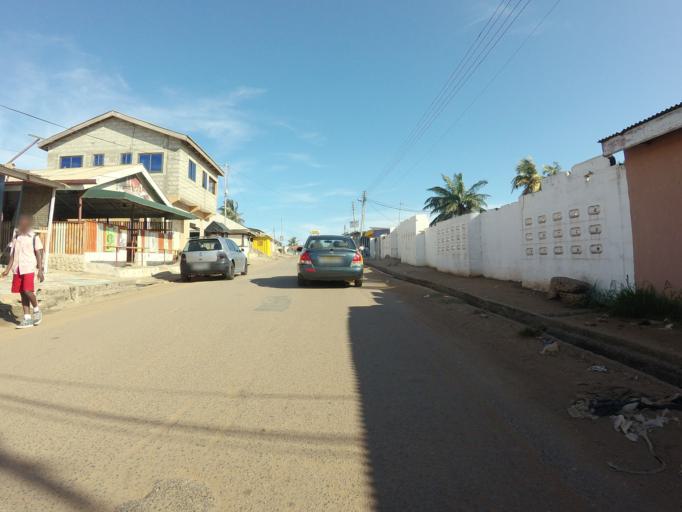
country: GH
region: Greater Accra
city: Nungua
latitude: 5.5909
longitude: -0.0825
